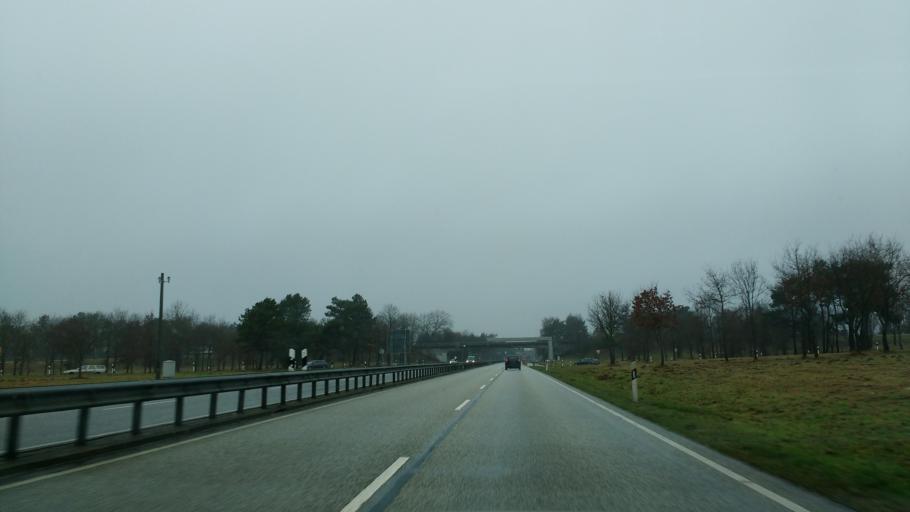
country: DE
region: Schleswig-Holstein
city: Westerronfeld
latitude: 54.2767
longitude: 9.6624
